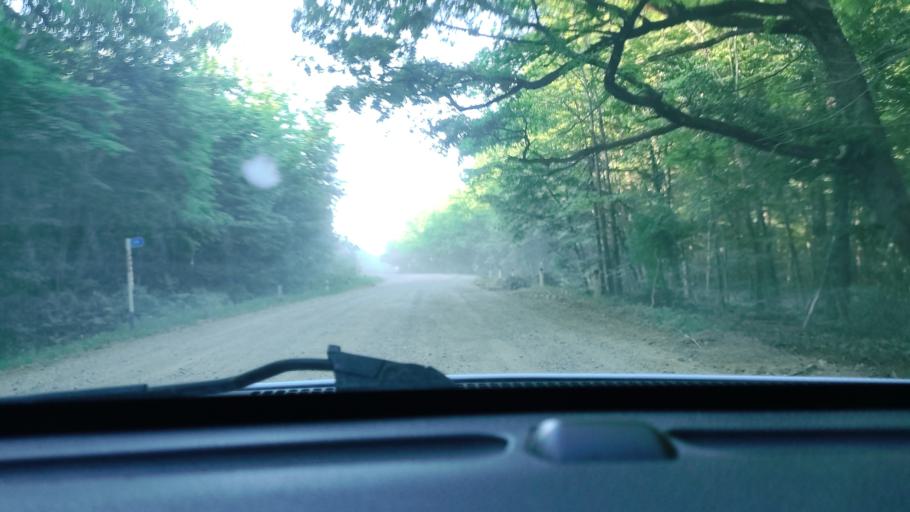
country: RU
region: Krasnodarskiy
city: Goryachiy Klyuch
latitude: 44.7140
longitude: 38.9912
